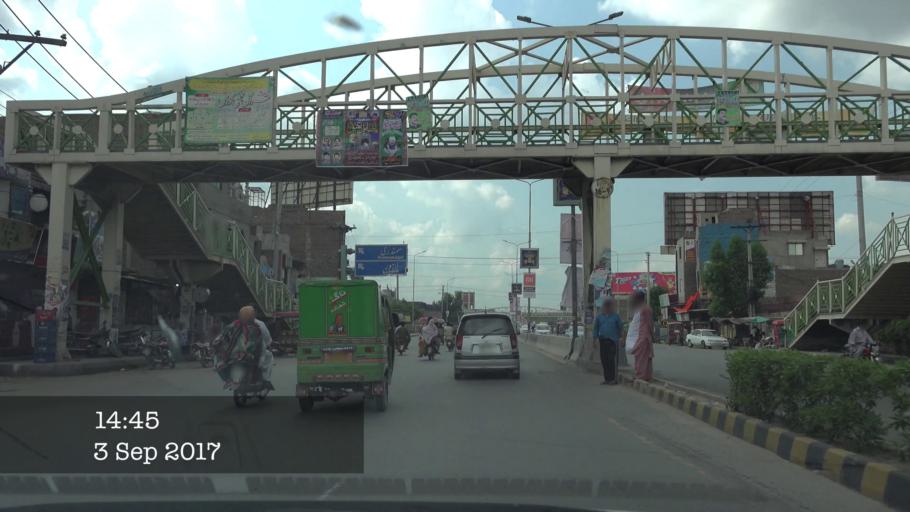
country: PK
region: Punjab
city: Faisalabad
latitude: 31.4189
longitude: 73.1057
